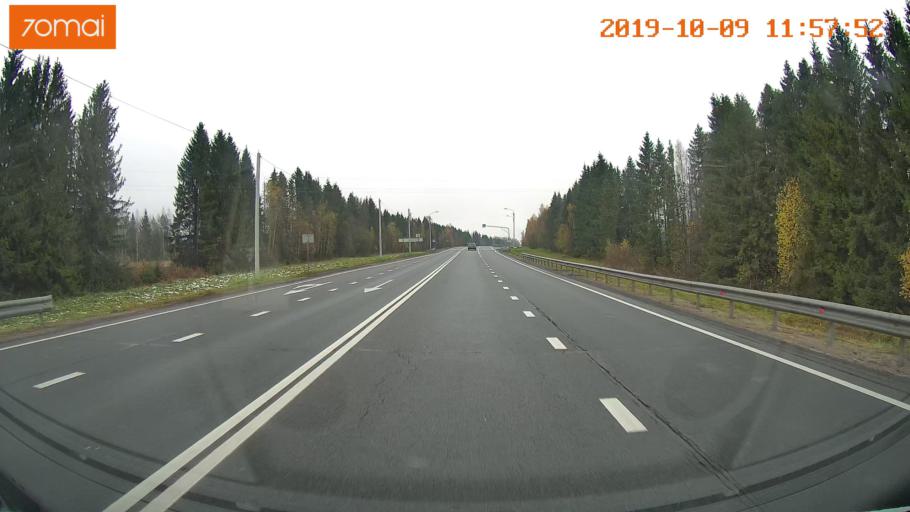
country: RU
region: Vologda
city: Gryazovets
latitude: 58.7262
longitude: 40.2950
